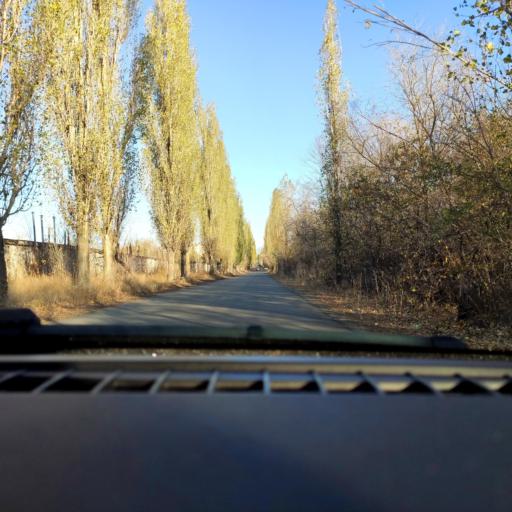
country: RU
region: Voronezj
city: Novaya Usman'
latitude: 51.6416
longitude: 39.3069
